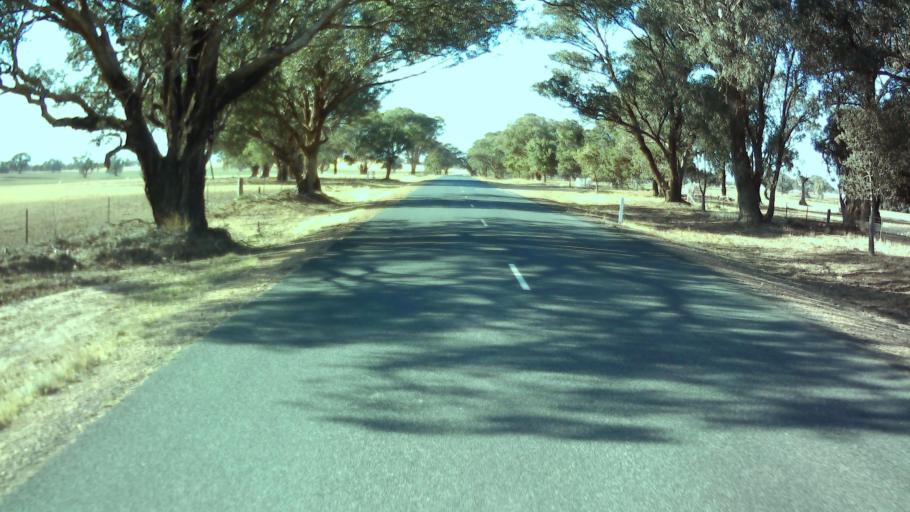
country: AU
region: New South Wales
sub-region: Weddin
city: Grenfell
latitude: -33.9621
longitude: 148.1402
